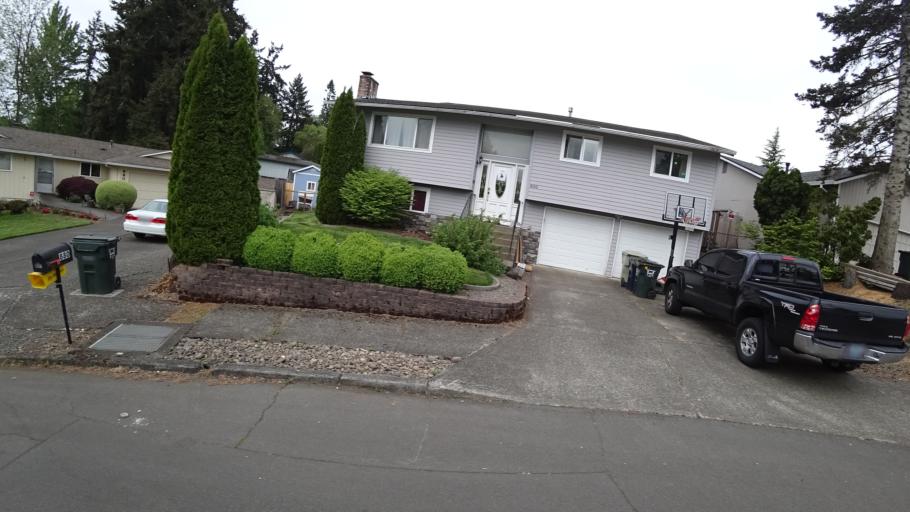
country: US
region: Oregon
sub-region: Washington County
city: Aloha
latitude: 45.5130
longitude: -122.8722
